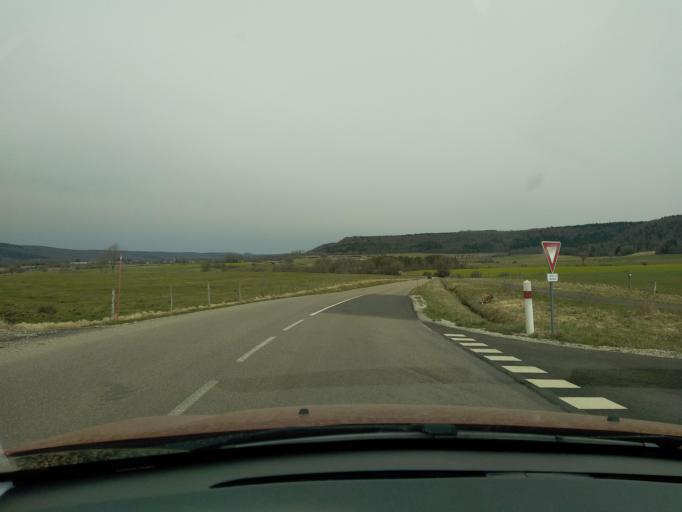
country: FR
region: Franche-Comte
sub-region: Departement du Jura
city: Clairvaux-les-Lacs
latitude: 46.6903
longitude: 5.7813
